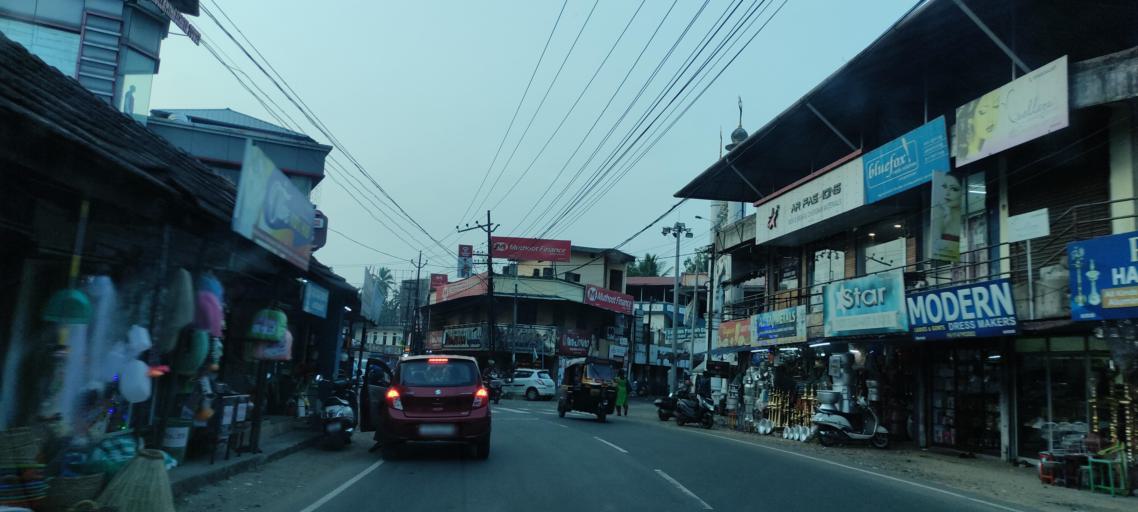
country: IN
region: Kerala
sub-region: Alappuzha
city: Mavelikara
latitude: 9.3231
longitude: 76.5338
